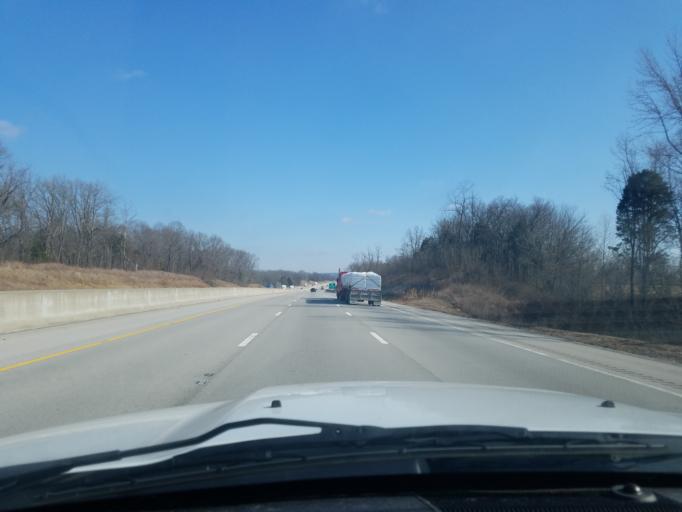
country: US
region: Kentucky
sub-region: Barren County
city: Cave City
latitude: 37.0734
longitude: -86.0851
